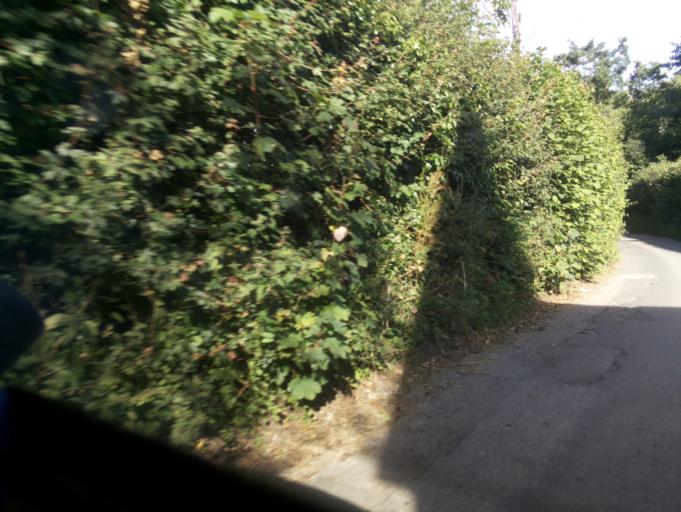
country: GB
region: England
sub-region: South Gloucestershire
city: Bitton
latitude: 51.4359
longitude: -2.4270
